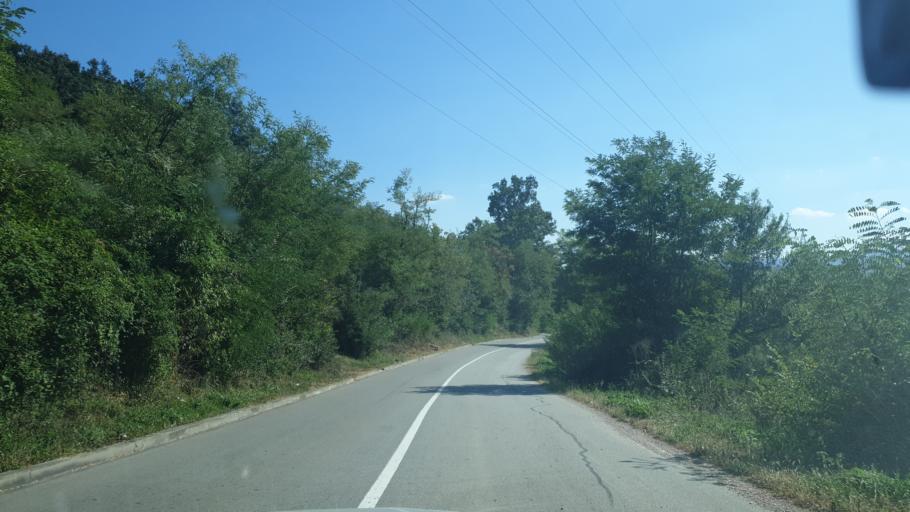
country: RS
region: Central Serbia
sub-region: Kolubarski Okrug
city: Mionica
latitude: 44.1968
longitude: 20.0242
